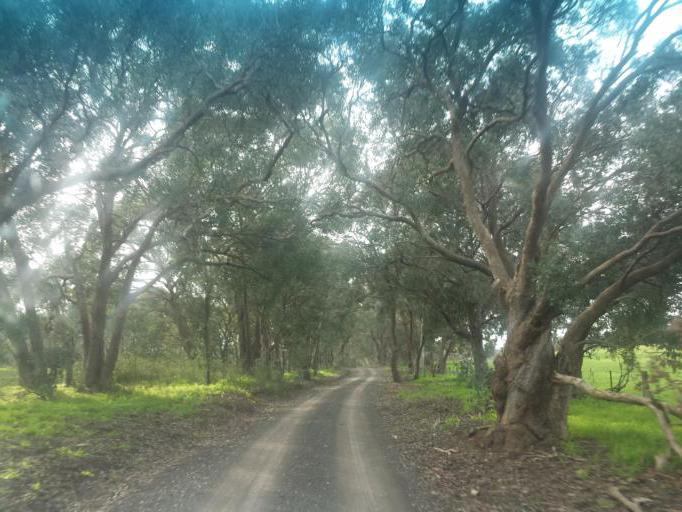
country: AU
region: Victoria
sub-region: Murrindindi
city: Kinglake West
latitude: -37.0264
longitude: 145.2502
